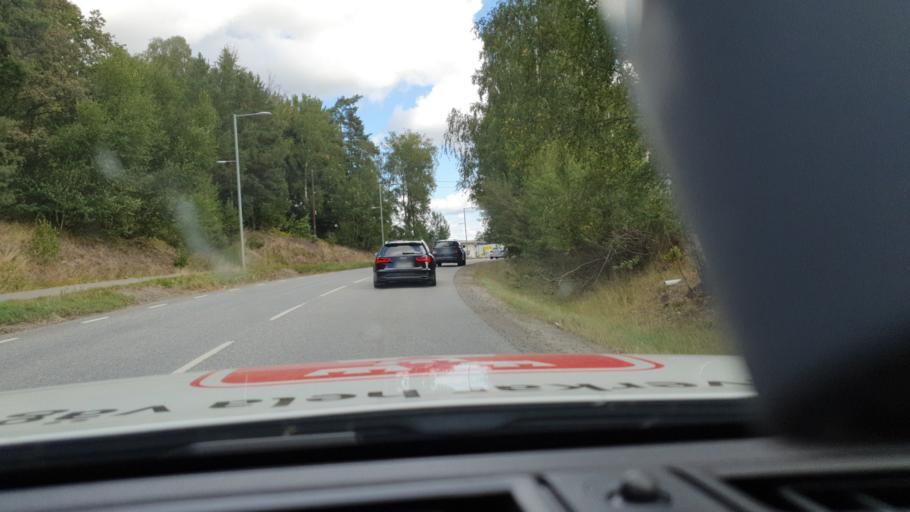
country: SE
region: Stockholm
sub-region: Osterakers Kommun
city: Akersberga
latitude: 59.4851
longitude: 18.2734
